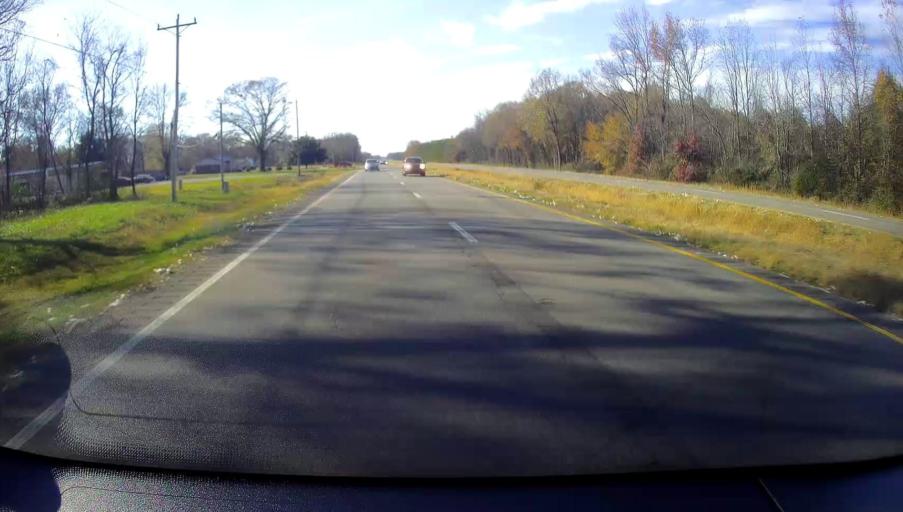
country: US
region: Alabama
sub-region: Morgan County
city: Trinity
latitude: 34.6491
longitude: -87.1938
